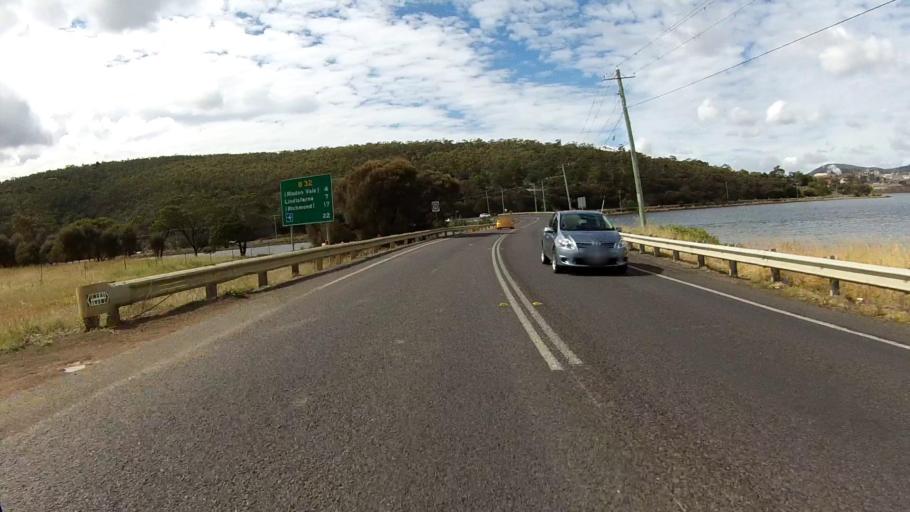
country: AU
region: Tasmania
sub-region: Glenorchy
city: Lutana
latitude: -42.8166
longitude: 147.3200
